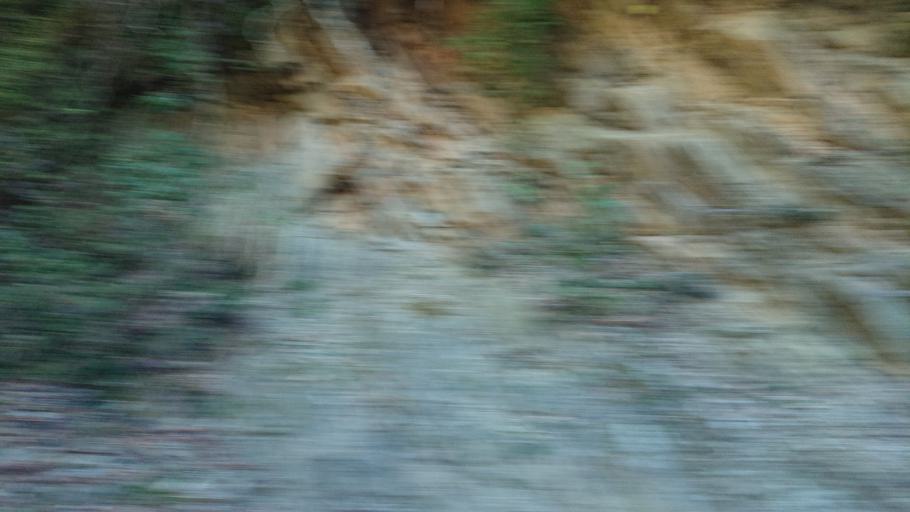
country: TW
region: Taiwan
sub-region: Hualien
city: Hualian
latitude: 24.3728
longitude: 121.3398
